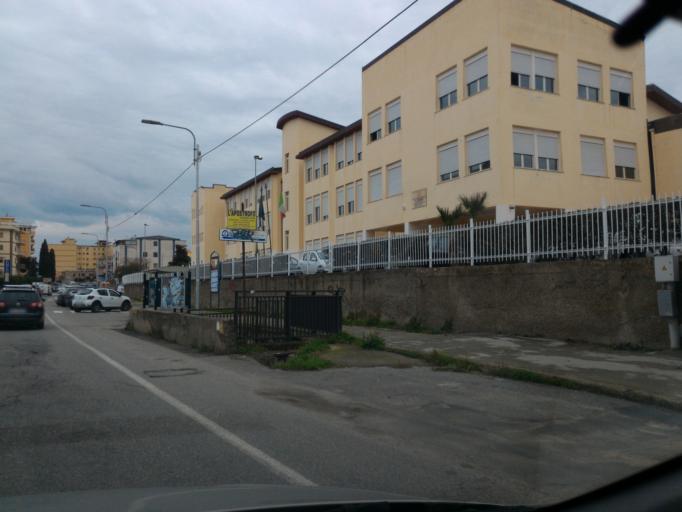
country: IT
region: Calabria
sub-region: Provincia di Catanzaro
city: Barone
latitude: 38.8301
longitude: 16.6270
